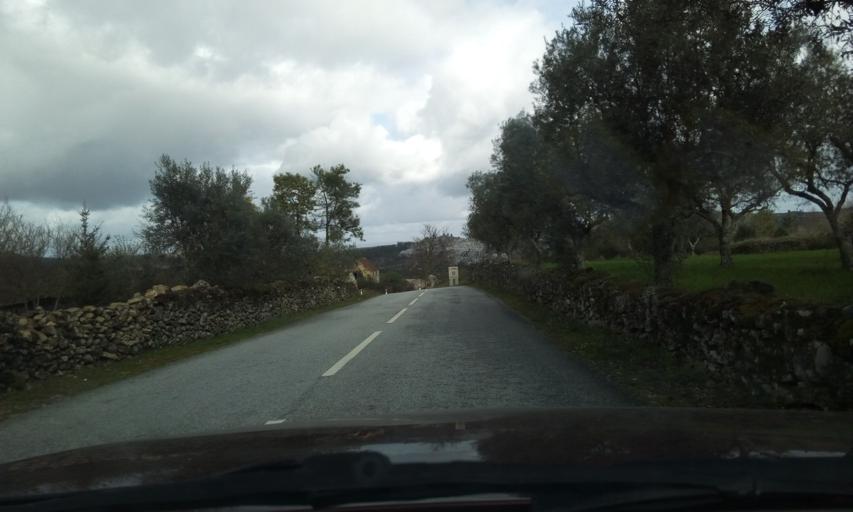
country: PT
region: Guarda
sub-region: Fornos de Algodres
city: Fornos de Algodres
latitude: 40.6536
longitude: -7.5500
